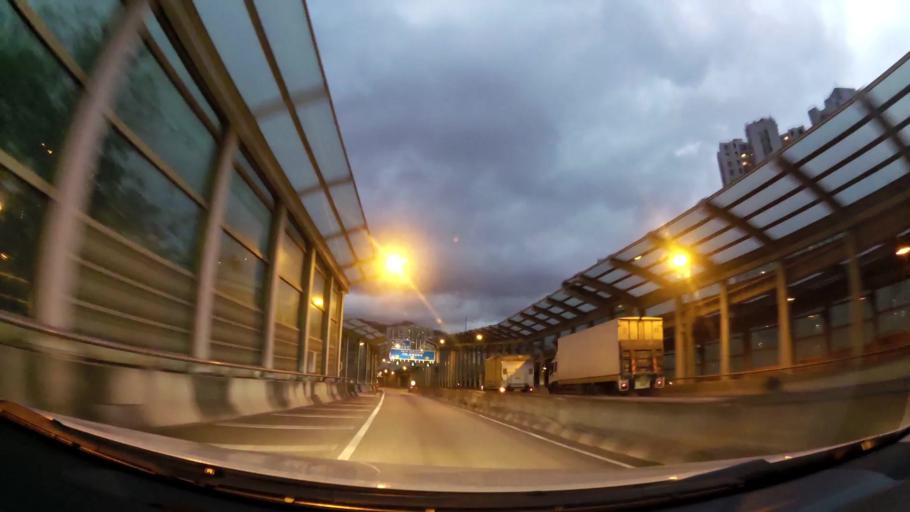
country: HK
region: Sha Tin
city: Sha Tin
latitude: 22.3733
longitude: 114.1749
